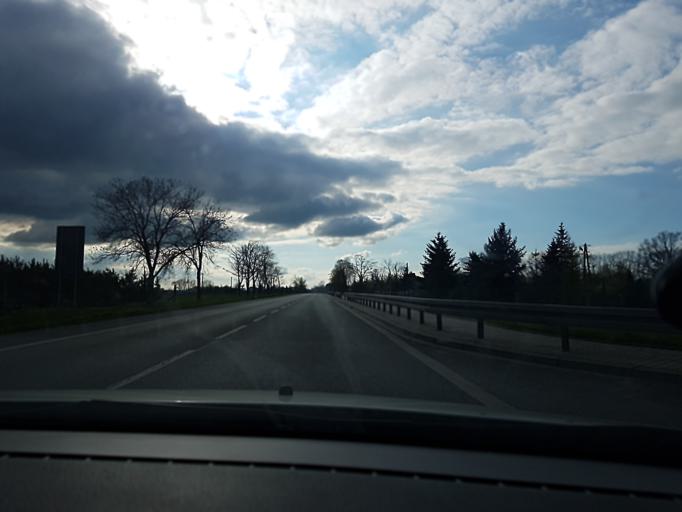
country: PL
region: Lodz Voivodeship
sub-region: powiat Lowicki
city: Lowicz
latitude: 52.1442
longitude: 19.8274
